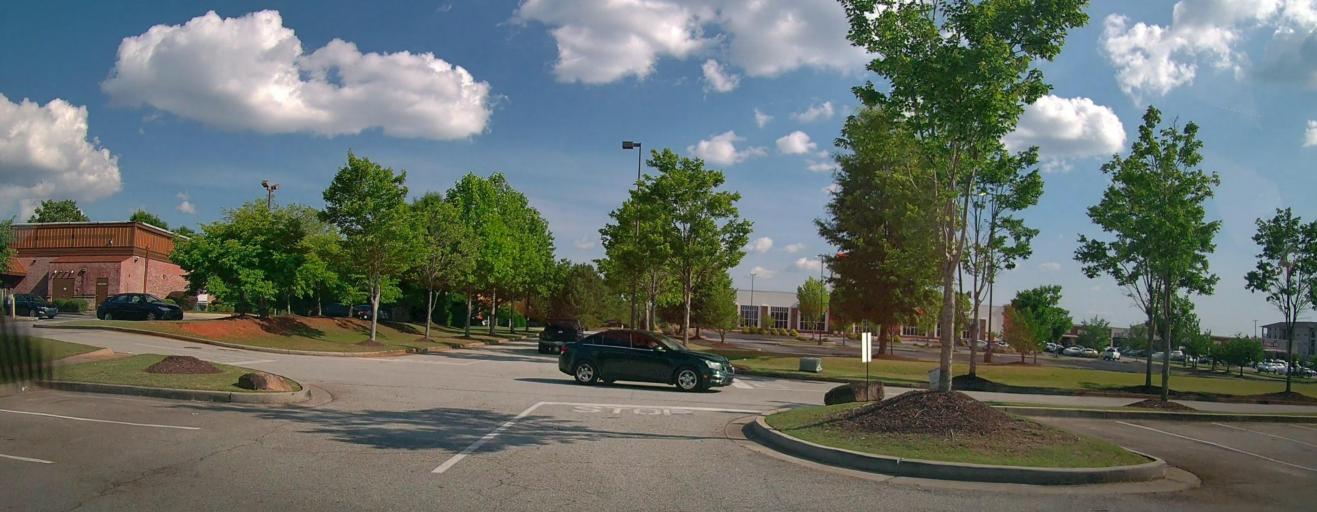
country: US
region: Georgia
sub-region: Henry County
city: McDonough
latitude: 33.4627
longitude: -84.2166
